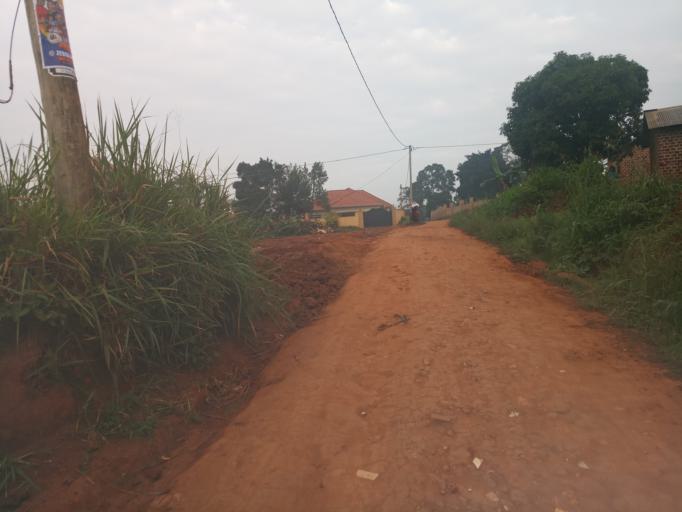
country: UG
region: Central Region
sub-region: Wakiso District
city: Kireka
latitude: 0.3901
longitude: 32.6367
